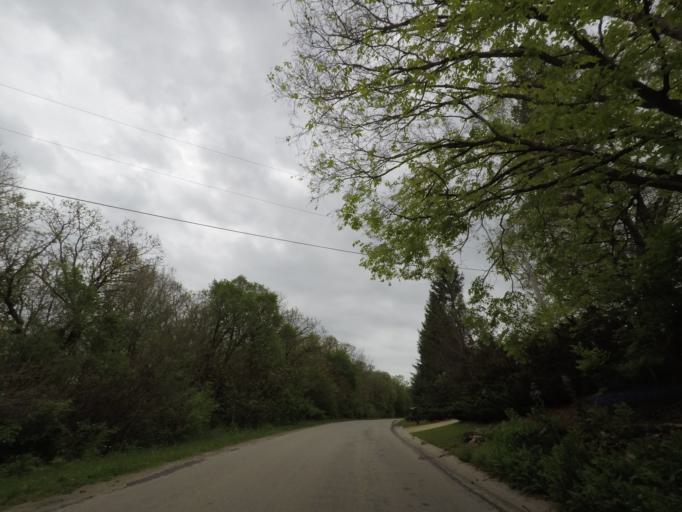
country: US
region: Illinois
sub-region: Winnebago County
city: Roscoe
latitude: 42.4129
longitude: -88.9774
